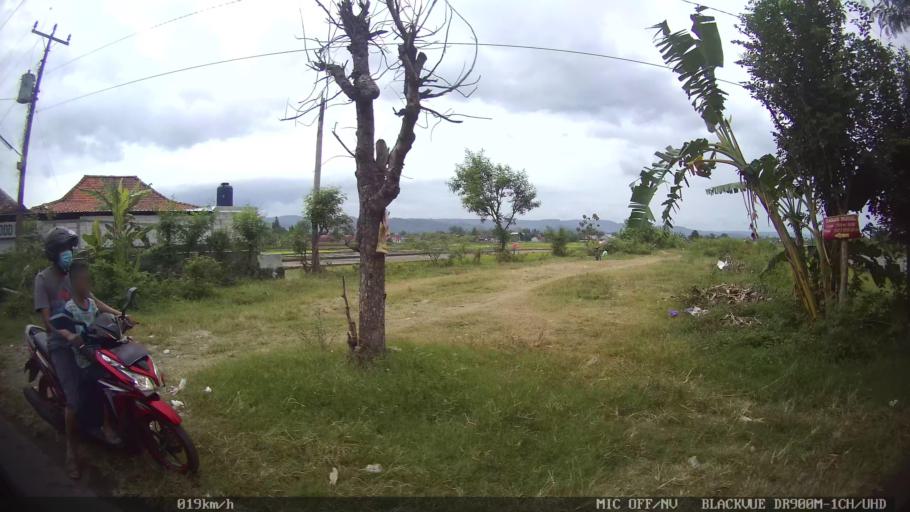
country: ID
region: Daerah Istimewa Yogyakarta
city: Sewon
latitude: -7.8360
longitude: 110.4179
